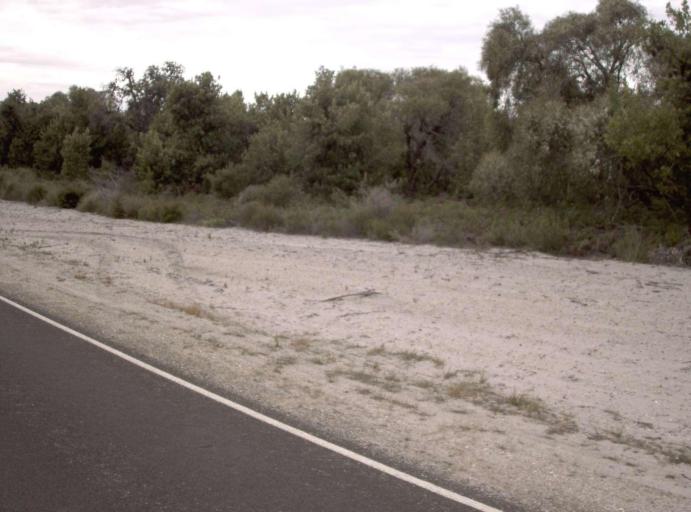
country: AU
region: Victoria
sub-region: Wellington
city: Sale
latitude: -38.1717
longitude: 147.3838
